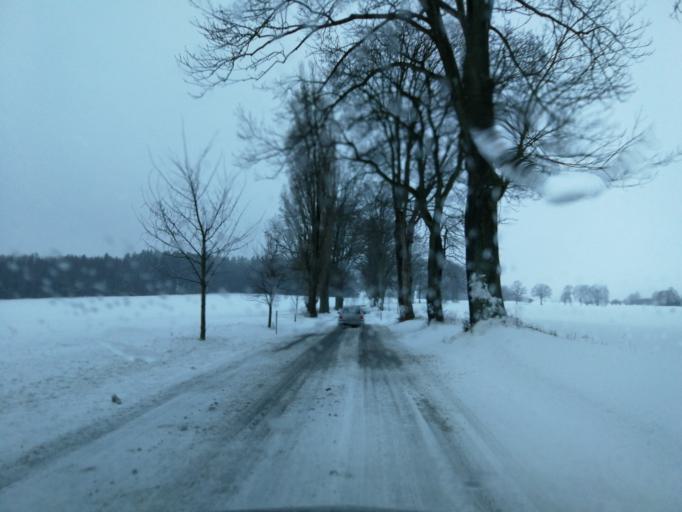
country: CZ
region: Vysocina
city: Heralec
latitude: 49.5343
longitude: 15.4401
